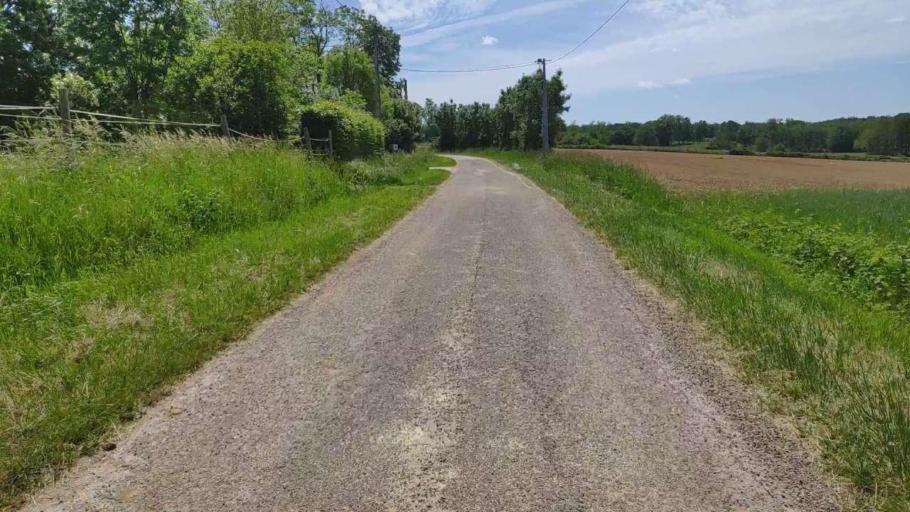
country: FR
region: Franche-Comte
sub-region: Departement du Jura
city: Bletterans
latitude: 46.7906
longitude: 5.3692
